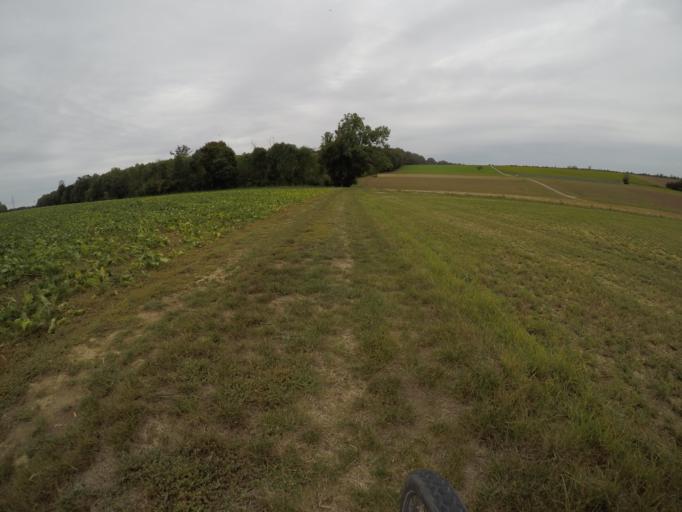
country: DE
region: Baden-Wuerttemberg
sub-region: Regierungsbezirk Stuttgart
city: Eberdingen
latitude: 48.8788
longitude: 8.9866
